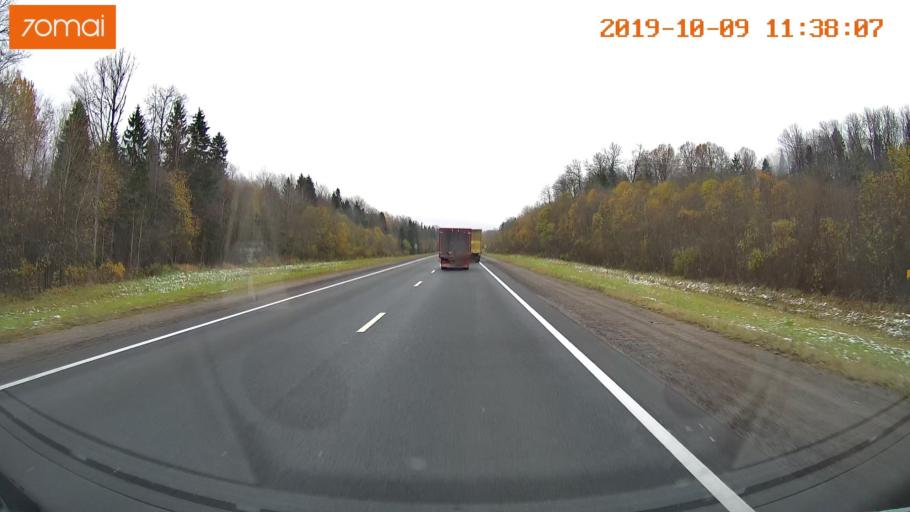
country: RU
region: Vologda
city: Gryazovets
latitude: 58.9717
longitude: 40.1529
